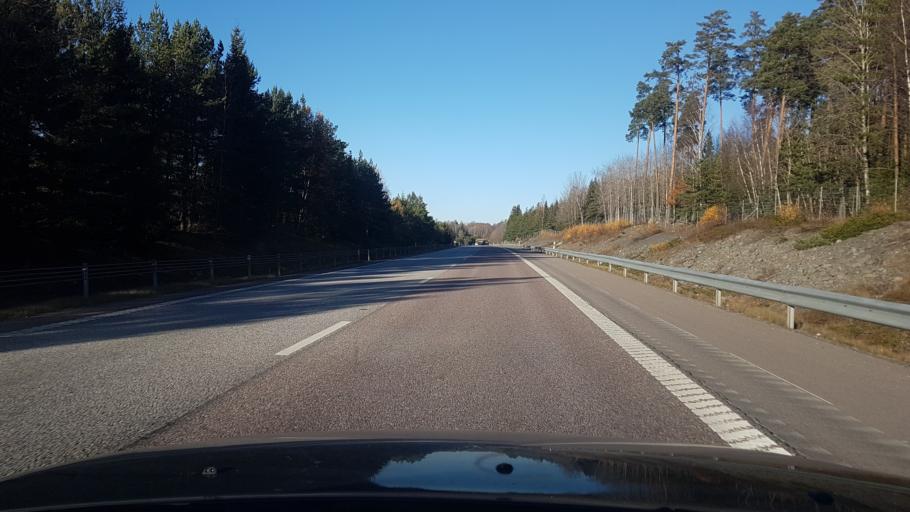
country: SE
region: Uppsala
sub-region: Uppsala Kommun
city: Alsike
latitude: 59.7724
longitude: 17.7866
